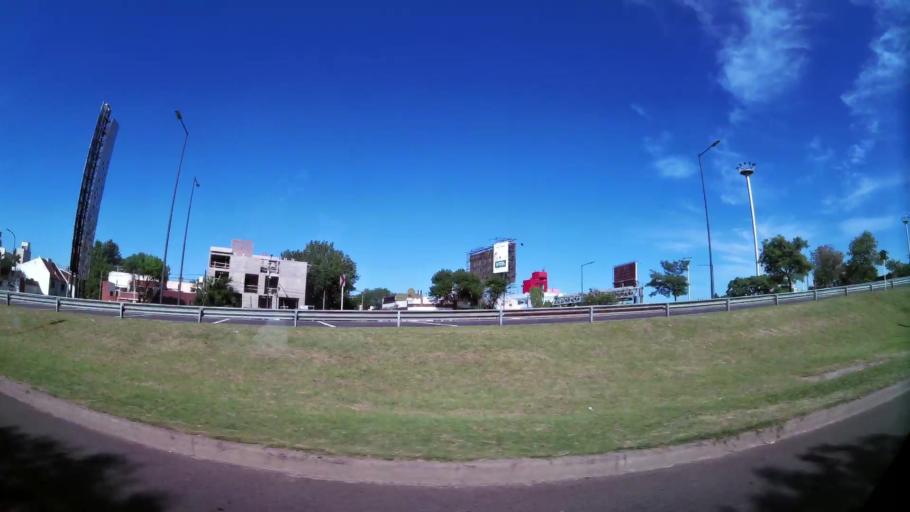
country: AR
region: Buenos Aires
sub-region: Partido de General San Martin
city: General San Martin
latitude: -34.5487
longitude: -58.4924
